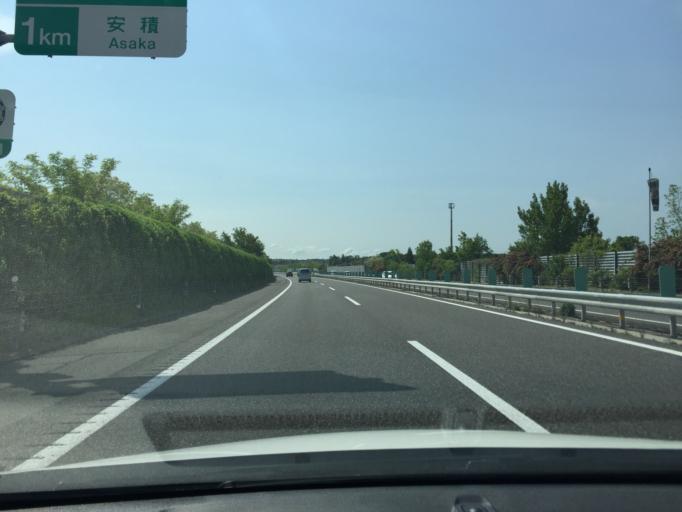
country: JP
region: Fukushima
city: Koriyama
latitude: 37.3616
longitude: 140.3133
